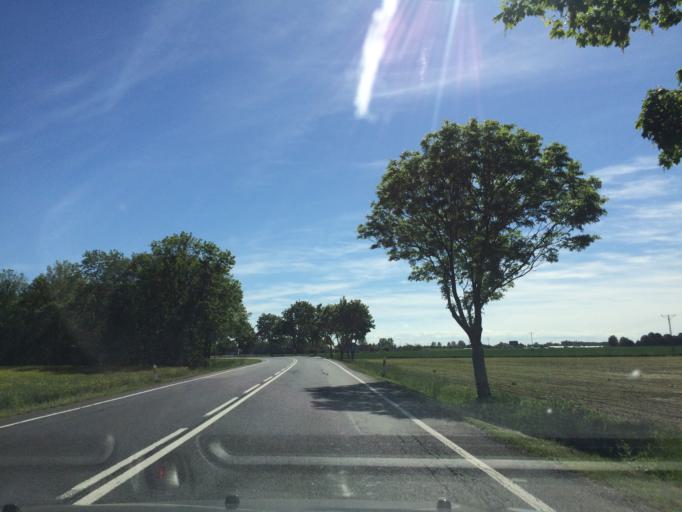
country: PL
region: Lower Silesian Voivodeship
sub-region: Powiat wroclawski
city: Gniechowice
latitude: 50.9611
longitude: 16.7888
